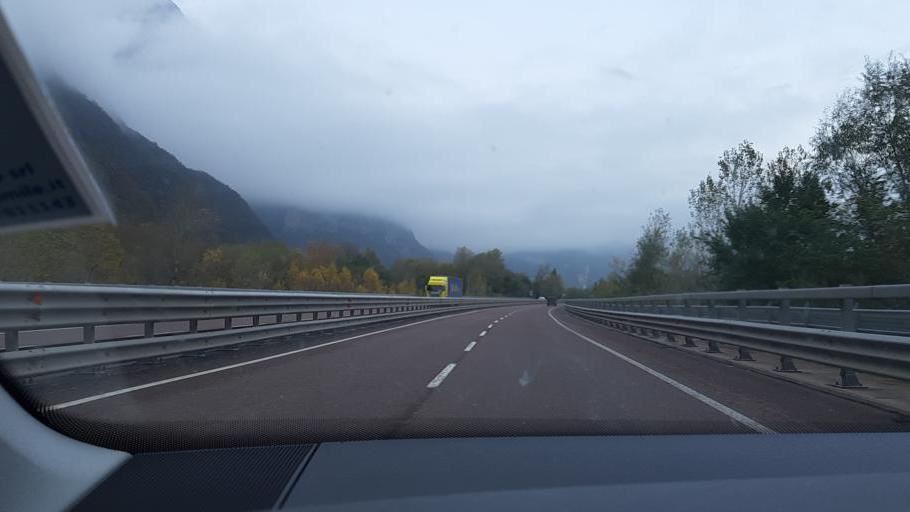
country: IT
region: Trentino-Alto Adige
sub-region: Provincia di Trento
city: Zambana
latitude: 46.1276
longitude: 11.0821
